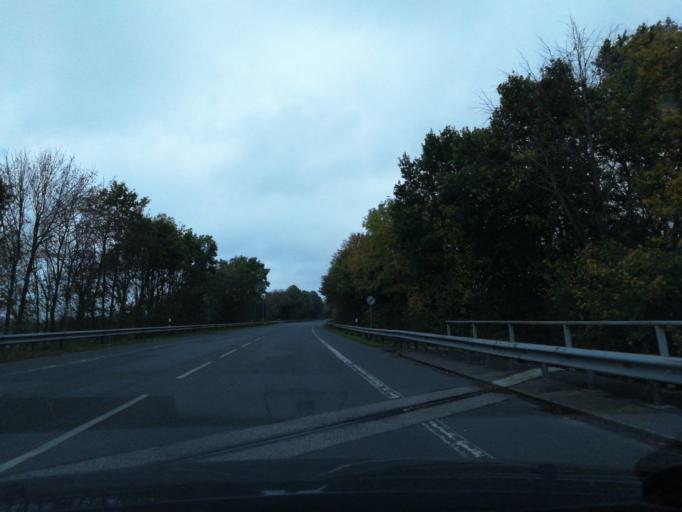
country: DE
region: Lower Saxony
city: Fedderwarden
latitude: 53.5508
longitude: 8.0473
